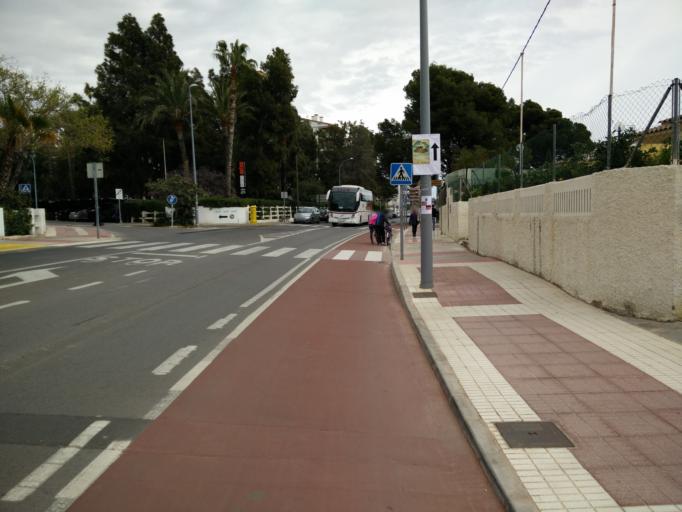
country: ES
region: Valencia
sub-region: Provincia de Castello
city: Benicassim
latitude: 40.0378
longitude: 0.0515
